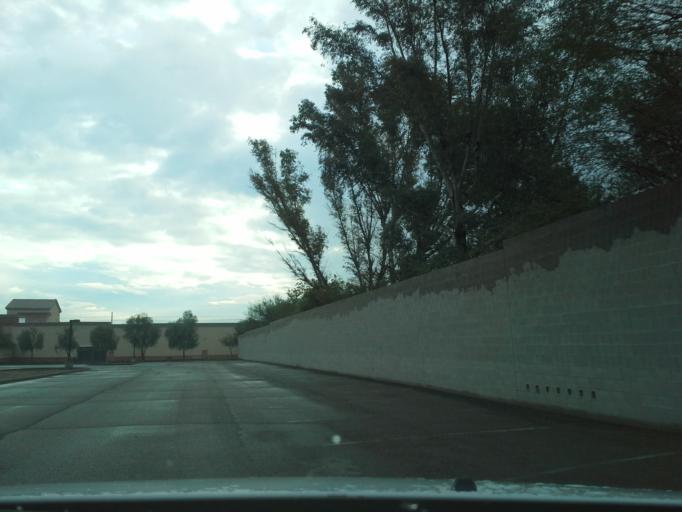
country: US
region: Arizona
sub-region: Maricopa County
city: Paradise Valley
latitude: 33.5810
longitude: -111.9812
